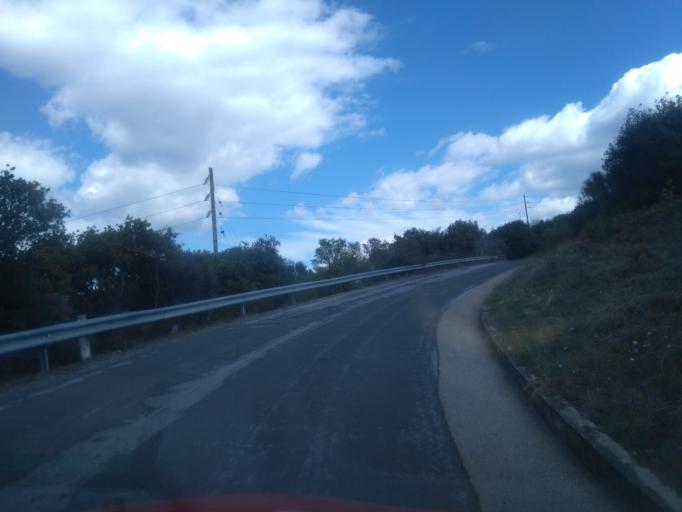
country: GR
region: Central Macedonia
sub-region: Nomos Thessalonikis
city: Asvestochori
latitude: 40.6373
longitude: 23.0163
